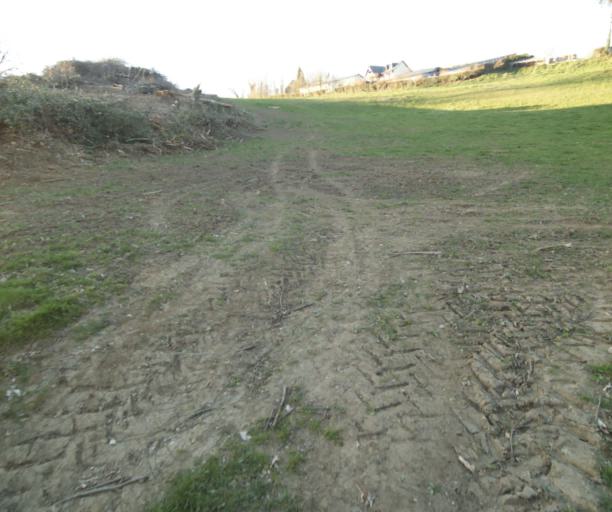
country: FR
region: Limousin
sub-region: Departement de la Correze
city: Saint-Clement
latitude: 45.3377
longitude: 1.7086
